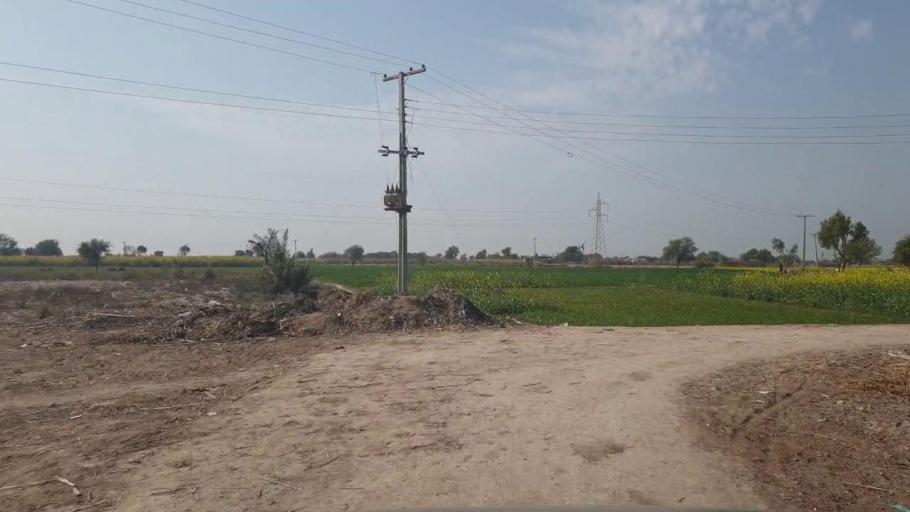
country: PK
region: Sindh
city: Tando Adam
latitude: 25.8222
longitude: 68.6429
